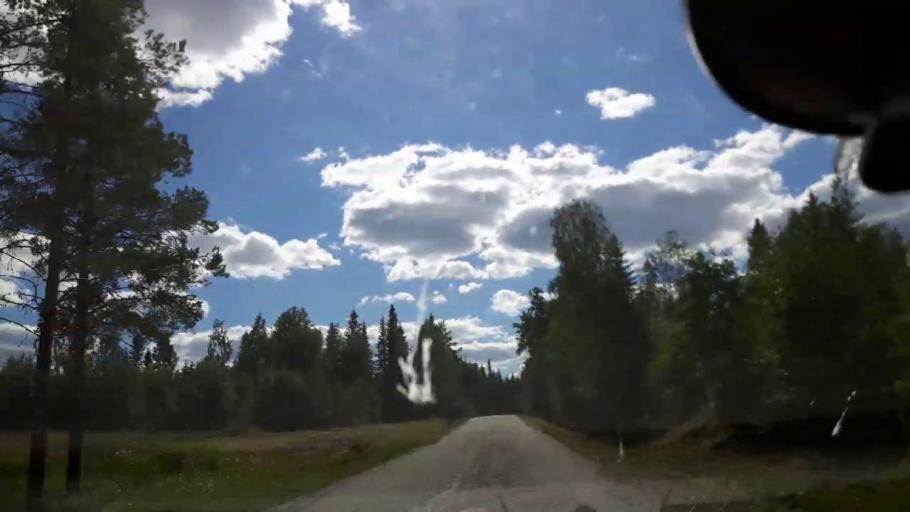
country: SE
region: Vaesternorrland
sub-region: Ange Kommun
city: Fransta
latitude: 62.7796
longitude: 15.9927
